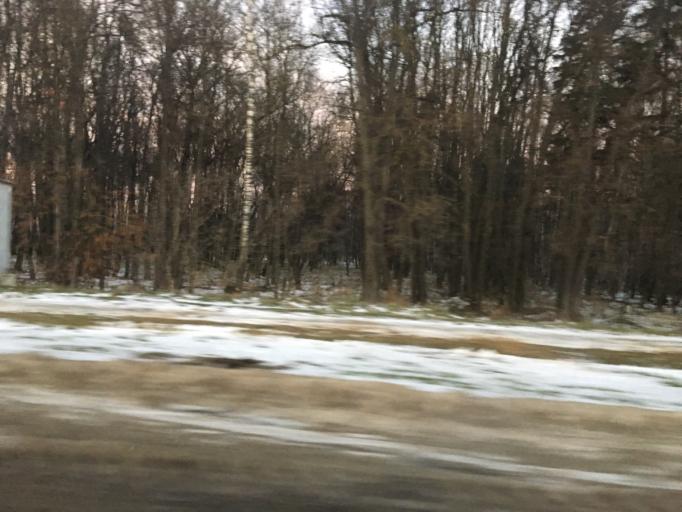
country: RU
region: Tula
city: Gorelki
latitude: 54.2515
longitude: 37.6109
